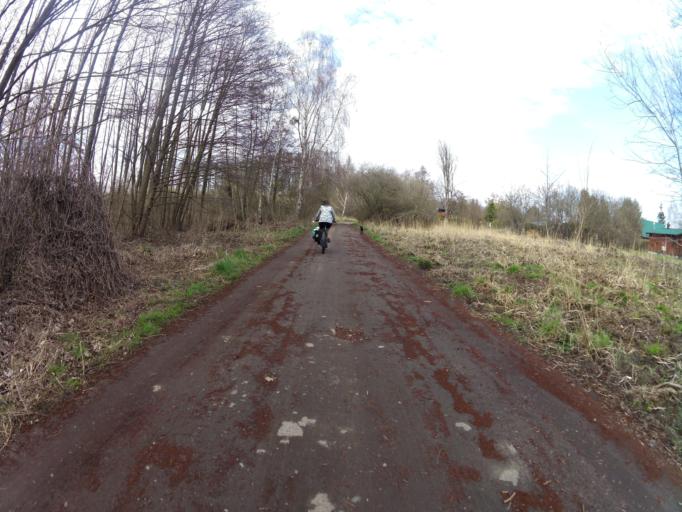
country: PL
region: West Pomeranian Voivodeship
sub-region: Powiat mysliborski
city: Mysliborz
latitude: 52.9536
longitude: 14.8700
